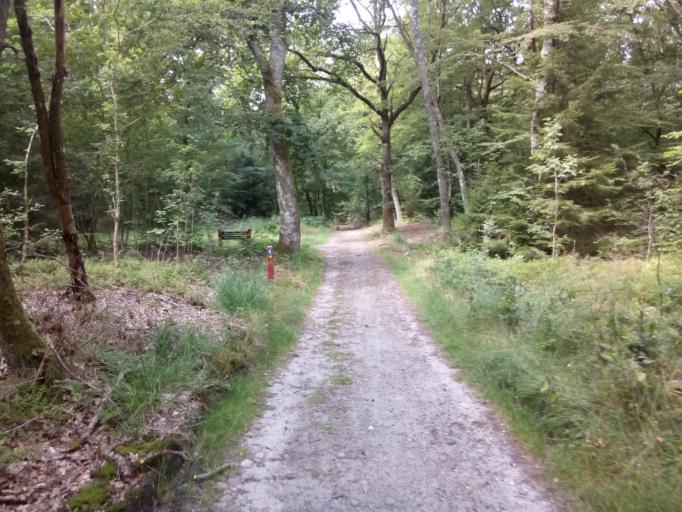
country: DK
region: Central Jutland
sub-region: Silkeborg Kommune
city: Svejbaek
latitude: 56.1080
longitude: 9.6887
